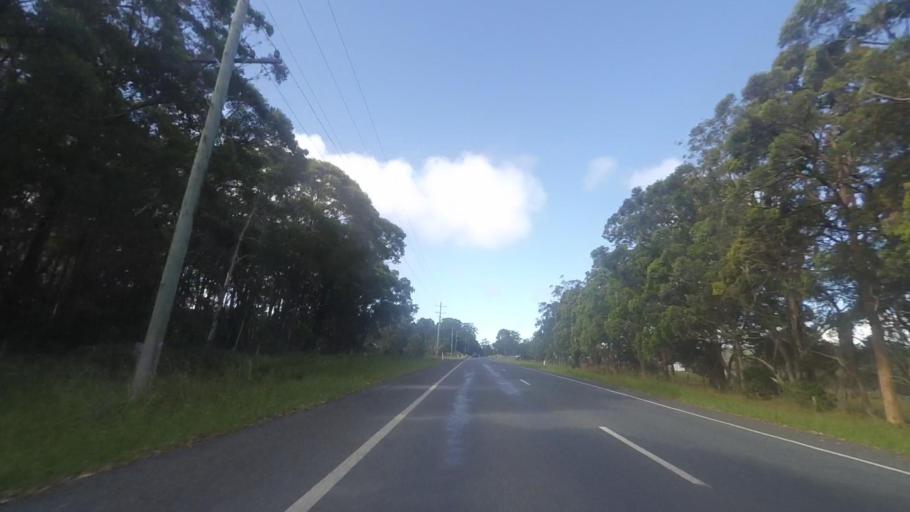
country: AU
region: New South Wales
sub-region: Great Lakes
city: Forster
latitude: -32.3601
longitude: 152.5032
